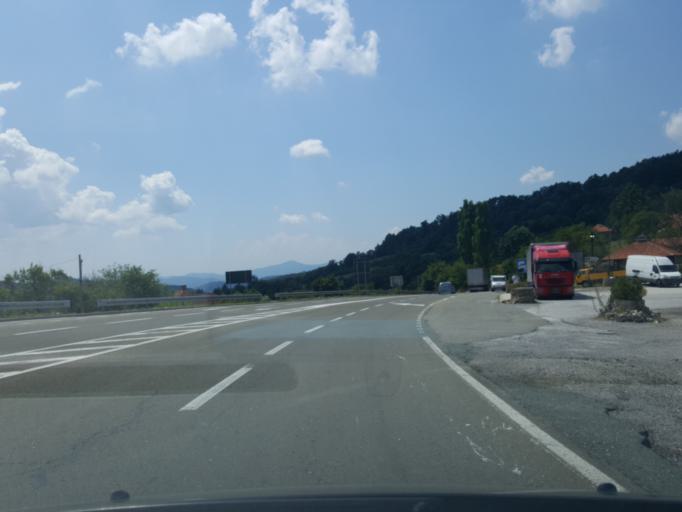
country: RS
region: Central Serbia
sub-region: Moravicki Okrug
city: Gornji Milanovac
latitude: 44.1213
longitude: 20.4834
